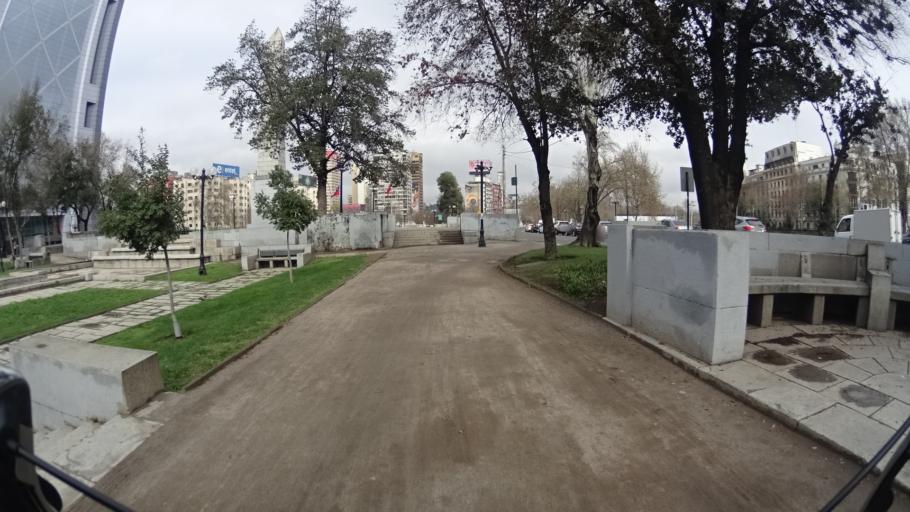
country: CL
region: Santiago Metropolitan
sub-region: Provincia de Santiago
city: Santiago
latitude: -33.4360
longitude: -70.6325
